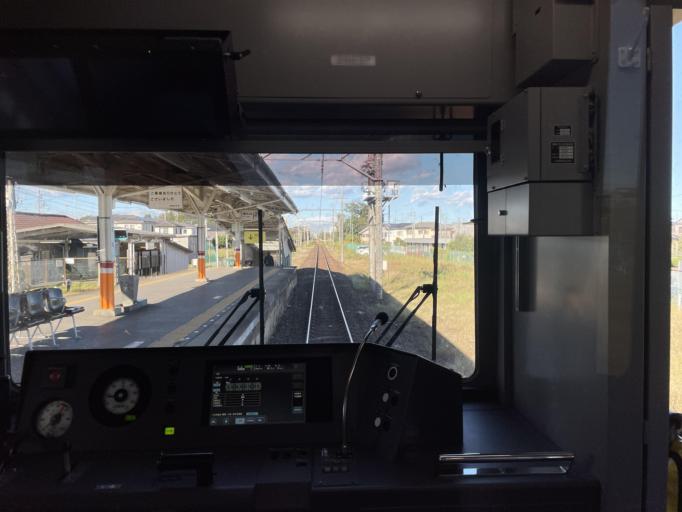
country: JP
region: Tochigi
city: Mibu
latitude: 36.4226
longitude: 139.8051
